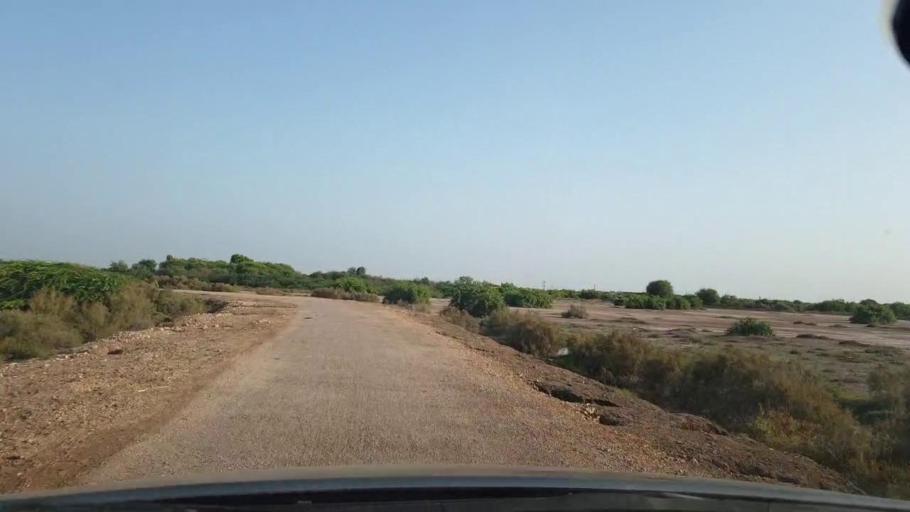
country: PK
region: Sindh
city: Naukot
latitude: 24.8155
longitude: 69.2013
